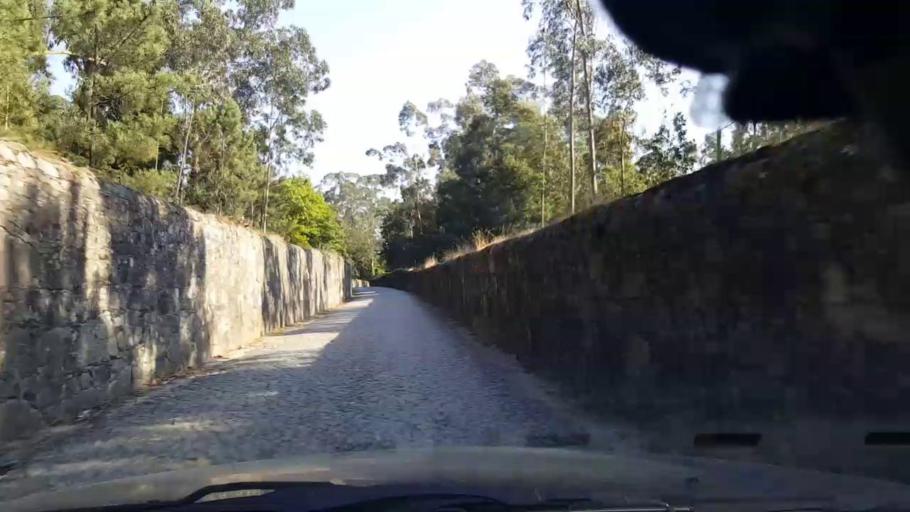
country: PT
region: Porto
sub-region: Vila do Conde
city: Arvore
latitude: 41.3446
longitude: -8.6891
